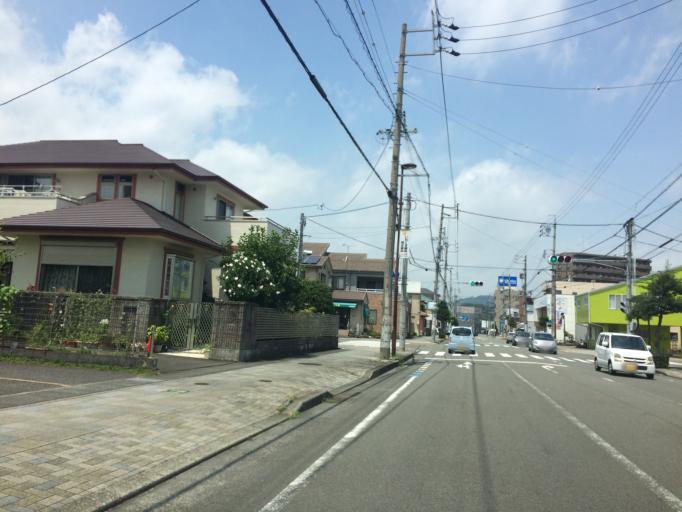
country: JP
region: Shizuoka
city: Fujieda
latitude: 34.8545
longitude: 138.2499
